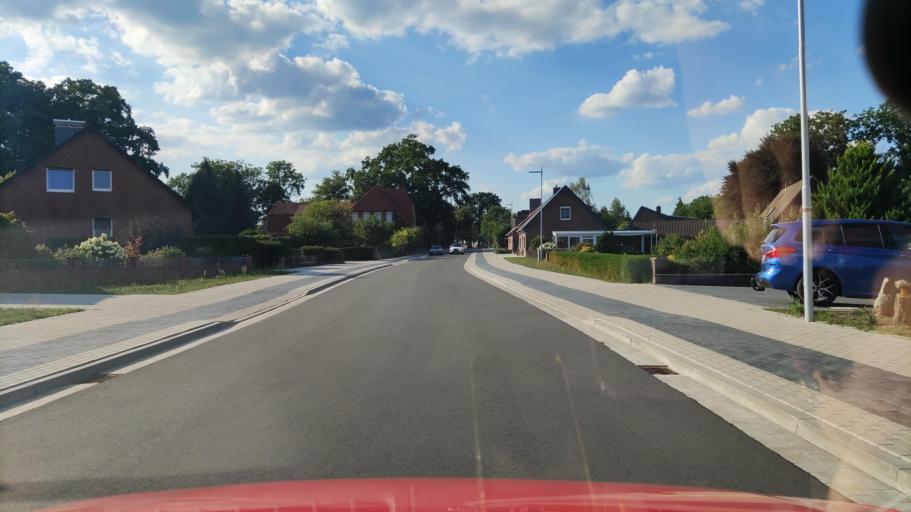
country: DE
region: Lower Saxony
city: Munster
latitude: 52.9816
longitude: 10.0934
